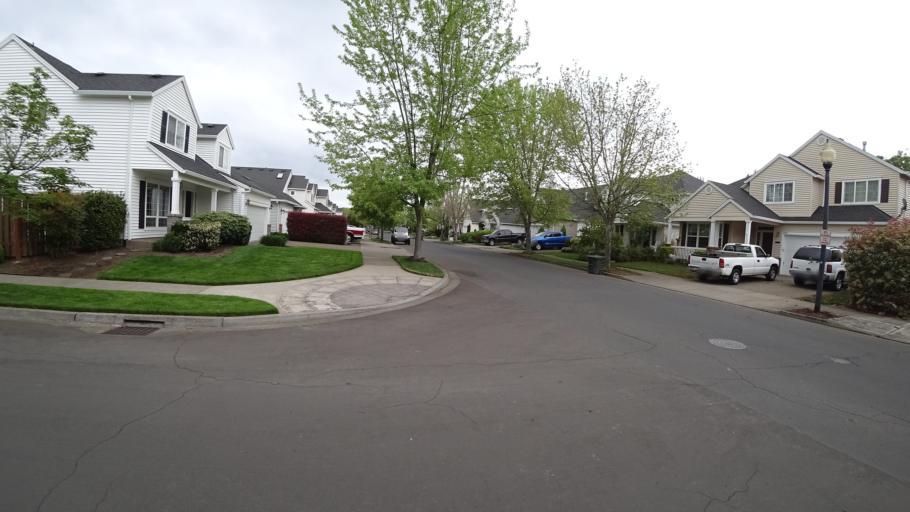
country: US
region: Oregon
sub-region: Washington County
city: Hillsboro
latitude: 45.5408
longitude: -122.9729
